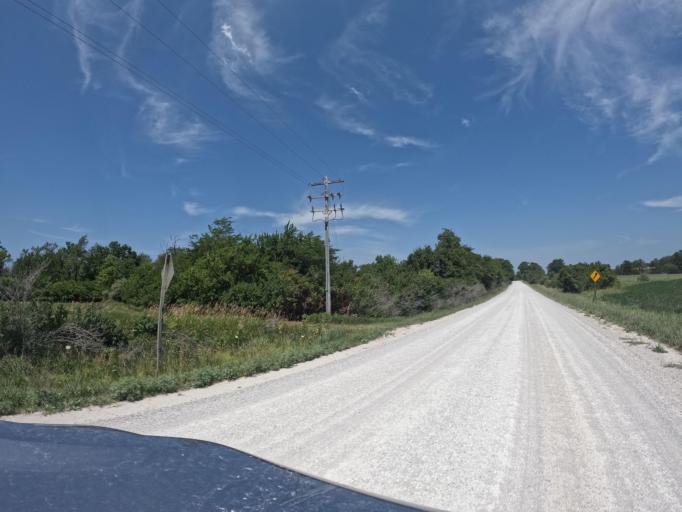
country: US
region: Iowa
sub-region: Henry County
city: Mount Pleasant
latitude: 40.9066
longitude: -91.5469
